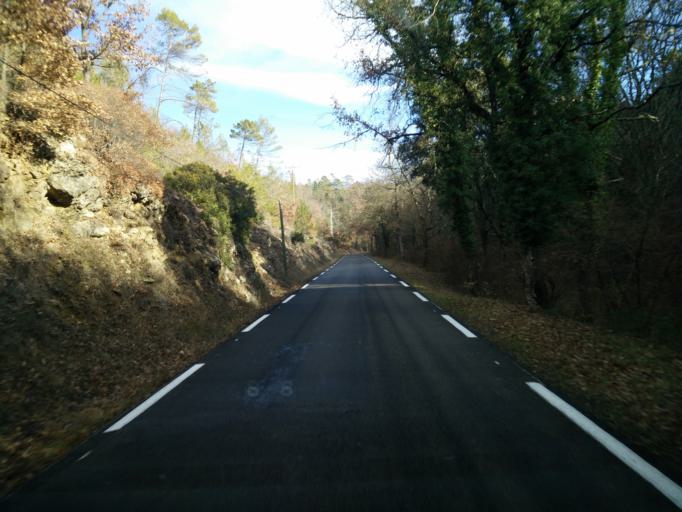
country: FR
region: Provence-Alpes-Cote d'Azur
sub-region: Departement du Var
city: Saint-Paul-en-Foret
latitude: 43.5726
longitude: 6.6727
